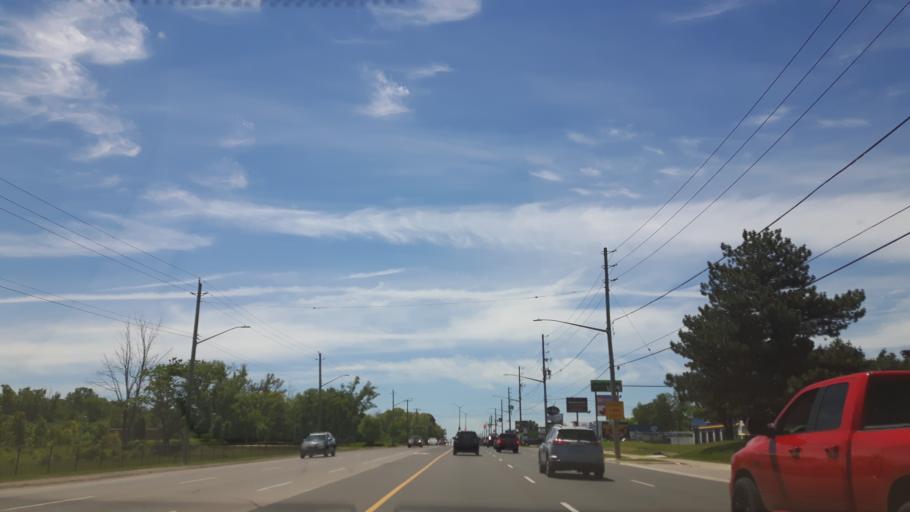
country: CA
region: Ontario
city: London
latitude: 42.9534
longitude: -81.2291
